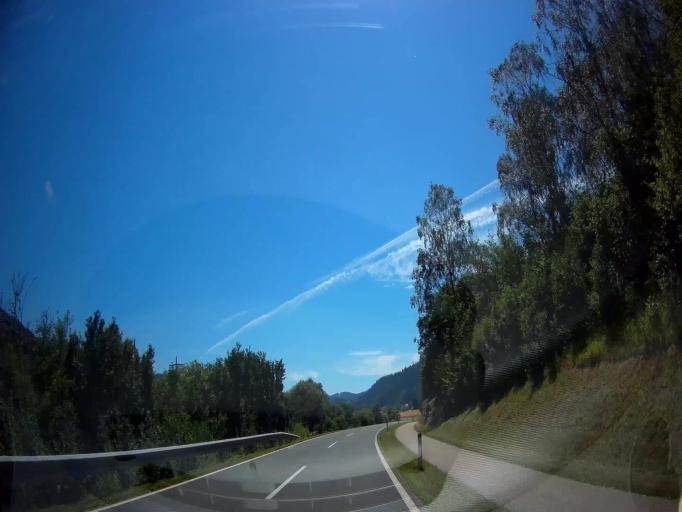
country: AT
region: Carinthia
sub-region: Politischer Bezirk Sankt Veit an der Glan
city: Micheldorf
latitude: 46.9272
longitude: 14.4276
